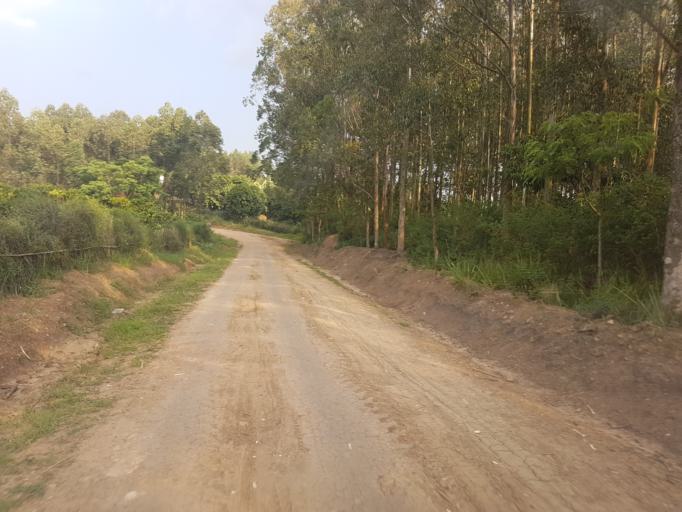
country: UG
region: Western Region
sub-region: Rukungiri District
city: Rukungiri
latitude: -0.6637
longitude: 29.8758
